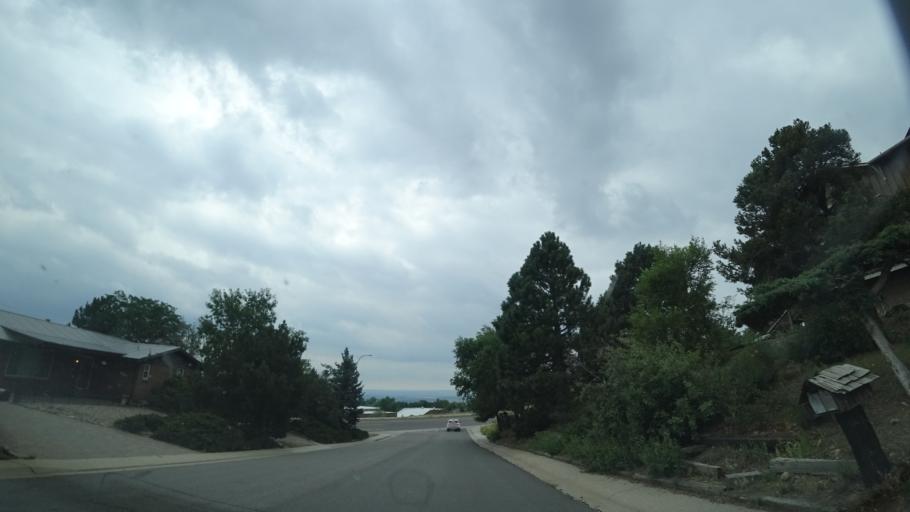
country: US
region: Colorado
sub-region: Jefferson County
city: West Pleasant View
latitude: 39.6924
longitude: -105.1505
